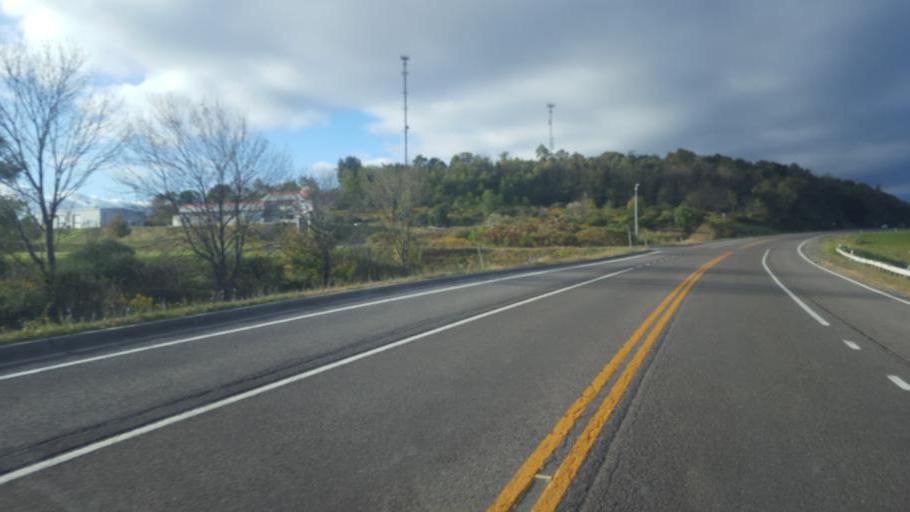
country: US
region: Maryland
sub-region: Allegany County
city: Frostburg
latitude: 39.6423
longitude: -78.9106
